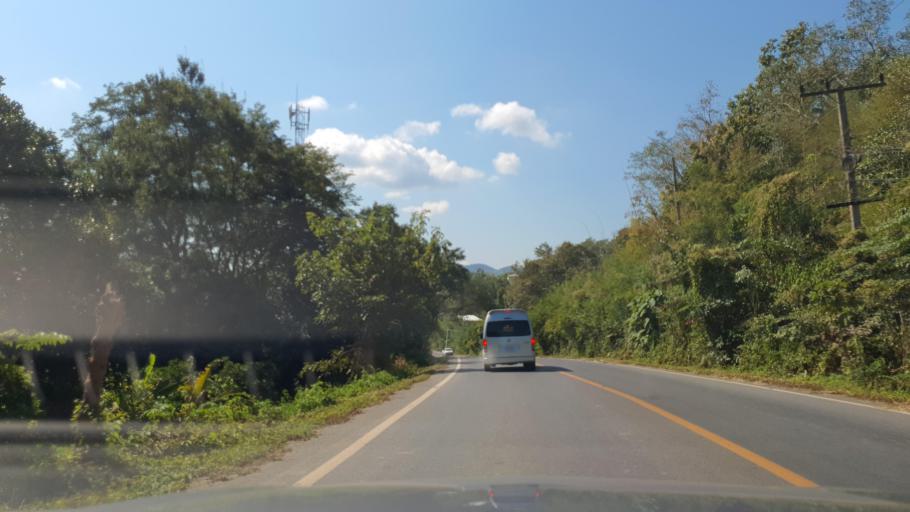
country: TH
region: Nan
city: Tha Wang Pha
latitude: 19.0779
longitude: 100.8711
